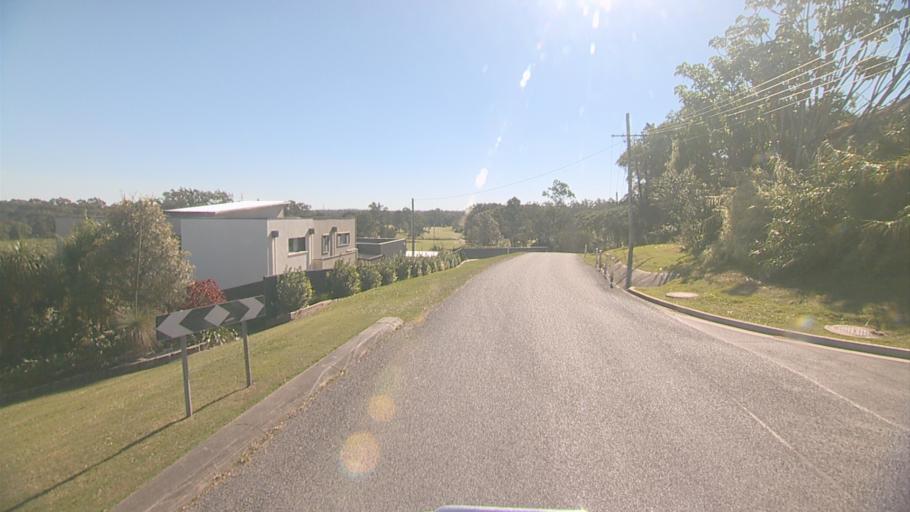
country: AU
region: Queensland
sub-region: Logan
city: Slacks Creek
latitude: -27.6651
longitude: 153.1622
